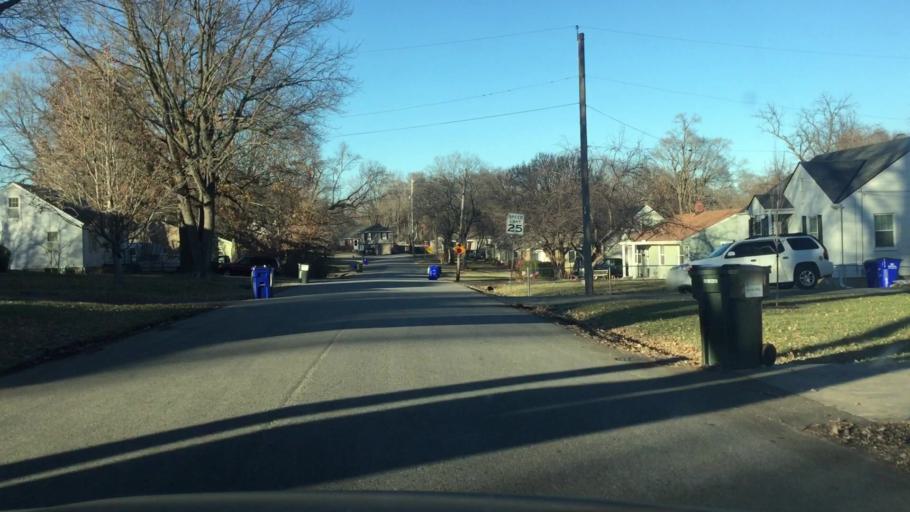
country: US
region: Kansas
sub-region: Johnson County
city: Shawnee
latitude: 39.0277
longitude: -94.7292
